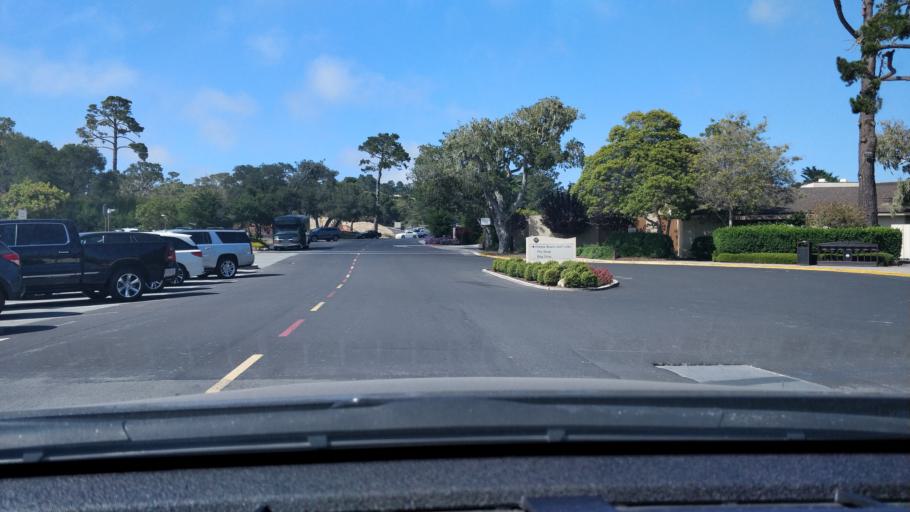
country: US
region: California
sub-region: Monterey County
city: Del Monte Forest
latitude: 36.5698
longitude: -121.9499
